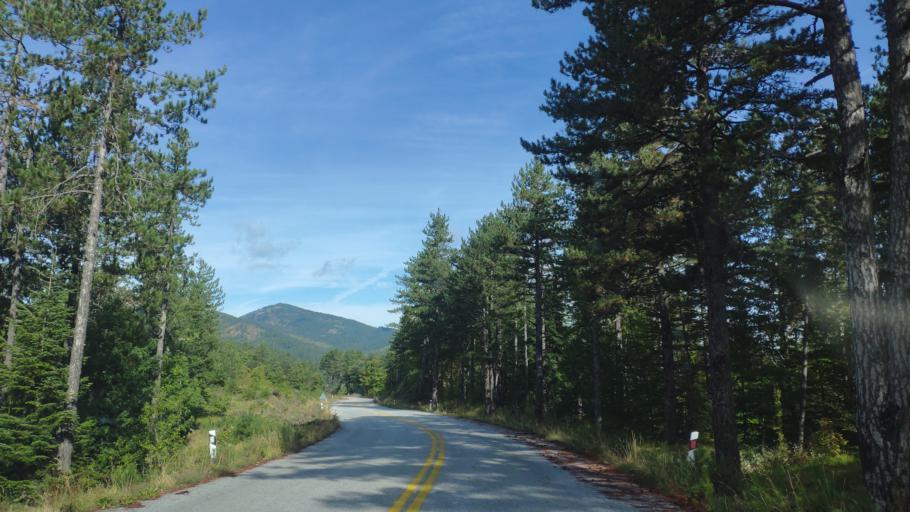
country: GR
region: West Macedonia
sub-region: Nomos Kastorias
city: Nestorio
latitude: 40.3670
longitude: 20.9457
